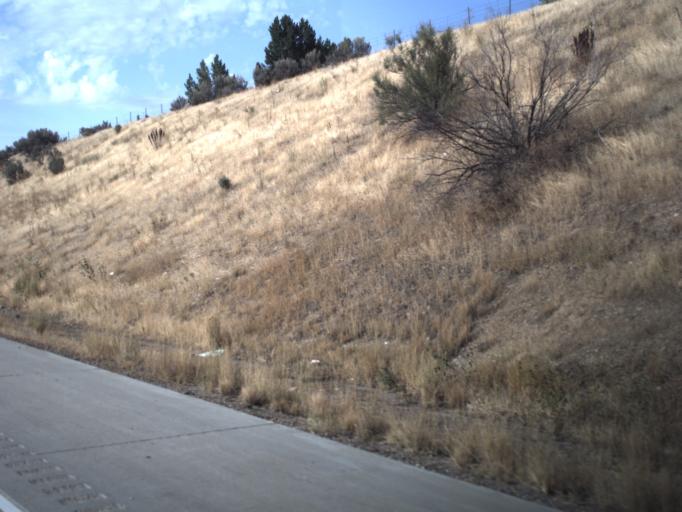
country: US
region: Utah
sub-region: Morgan County
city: Morgan
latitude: 41.0847
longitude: -111.7312
